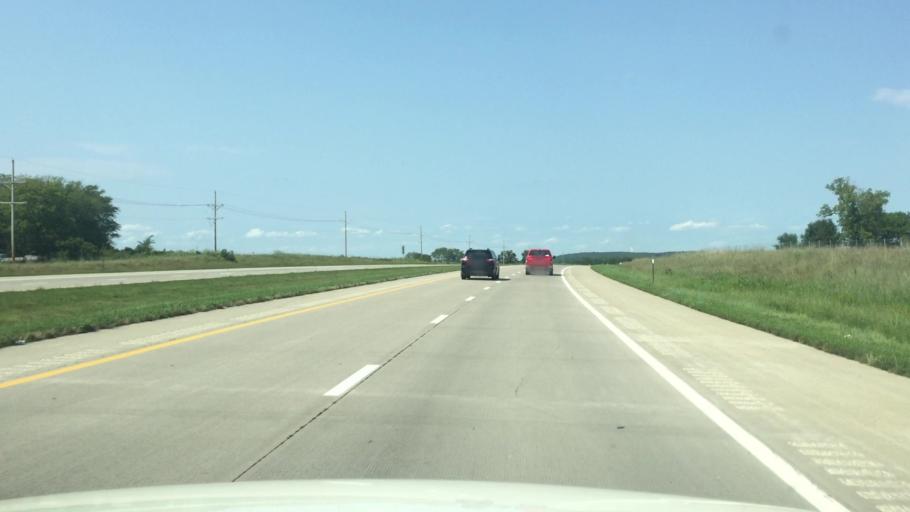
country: US
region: Kansas
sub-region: Linn County
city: Pleasanton
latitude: 38.2104
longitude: -94.7048
